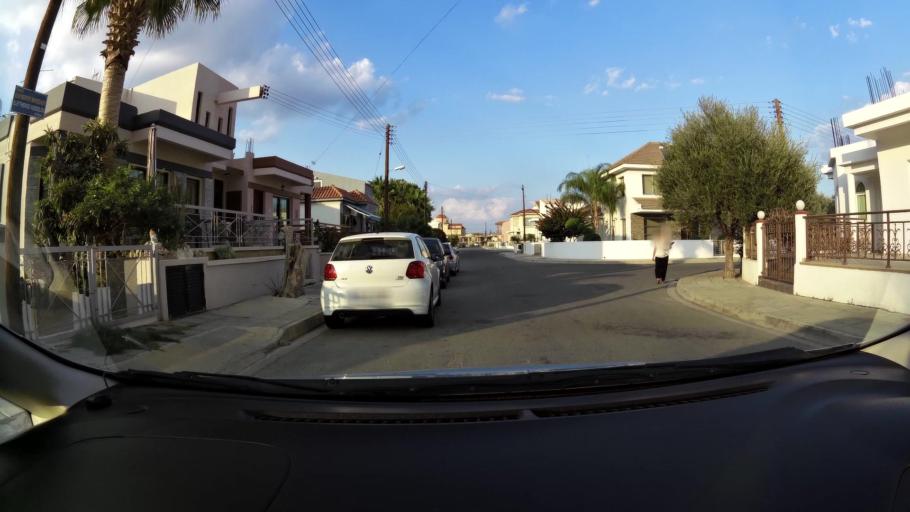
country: CY
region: Larnaka
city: Meneou
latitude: 34.8604
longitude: 33.5896
